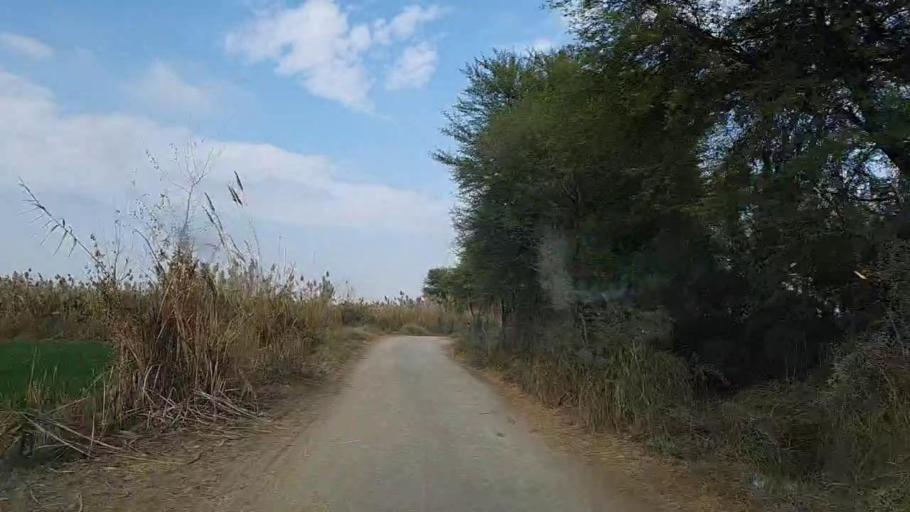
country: PK
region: Sindh
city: Sanghar
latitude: 26.2310
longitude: 69.0195
